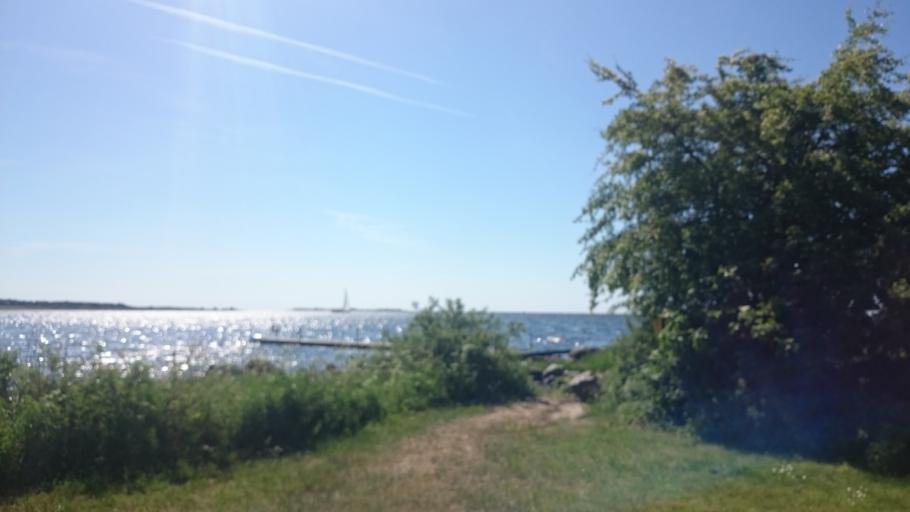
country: SE
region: Blekinge
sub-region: Solvesborgs Kommun
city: Soelvesborg
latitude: 56.0392
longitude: 14.5215
